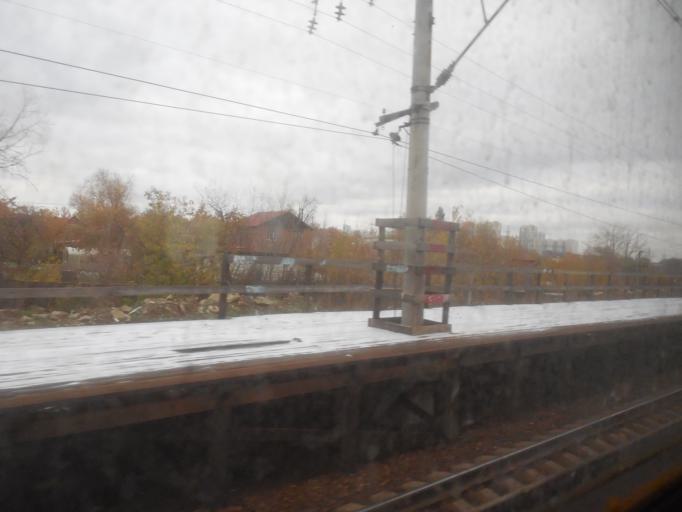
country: RU
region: Moscow
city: Novo-Peredelkino
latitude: 55.6839
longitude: 37.3198
